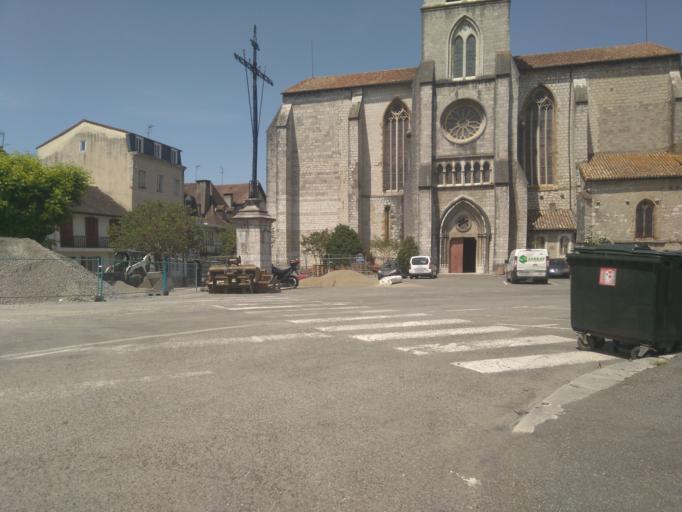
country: FR
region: Aquitaine
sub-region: Departement des Pyrenees-Atlantiques
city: Orthez
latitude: 43.4889
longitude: -0.7754
